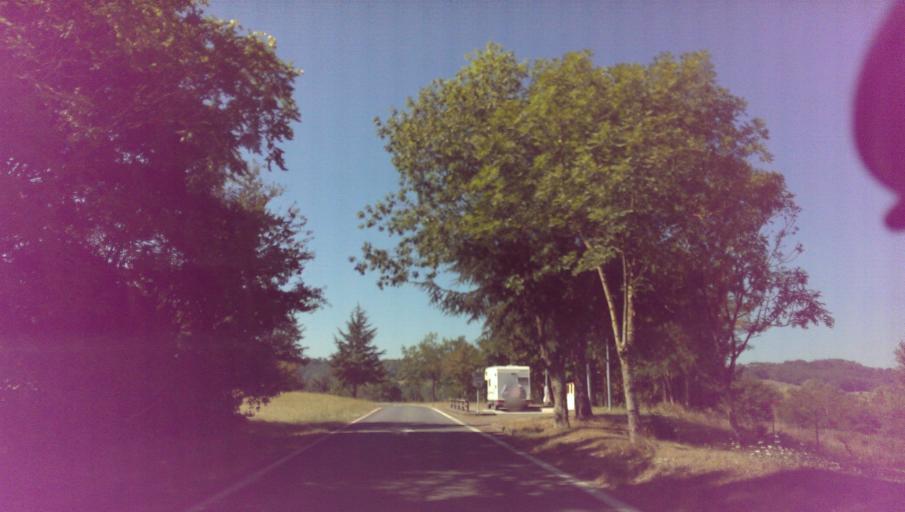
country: FR
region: Aquitaine
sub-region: Departement du Lot-et-Garonne
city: Sainte-Colombe-en-Bruilhois
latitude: 44.2000
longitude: 0.5066
